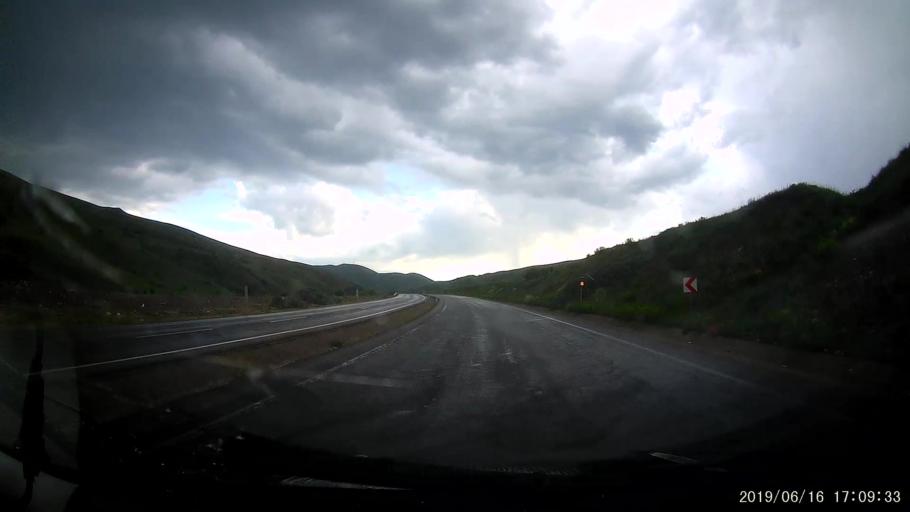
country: TR
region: Erzurum
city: Askale
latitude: 39.8933
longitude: 40.6485
